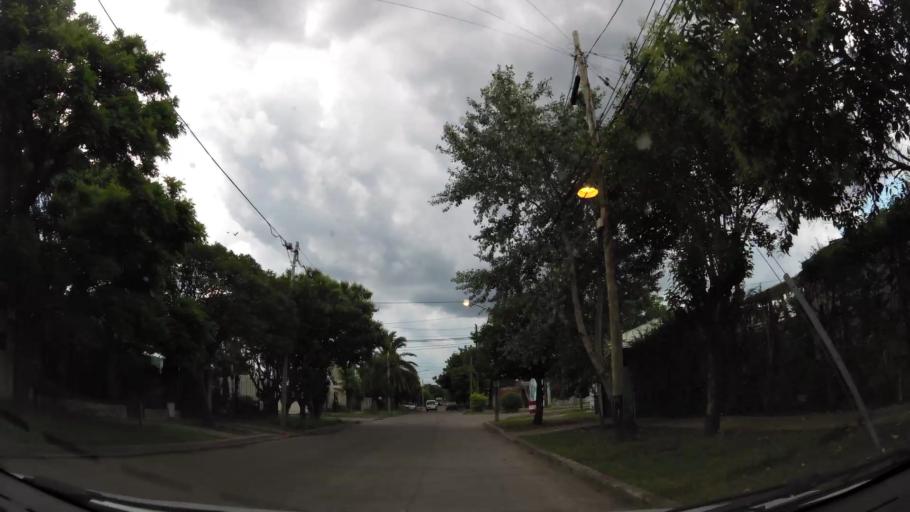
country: AR
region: Buenos Aires
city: Ituzaingo
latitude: -34.6417
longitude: -58.6849
